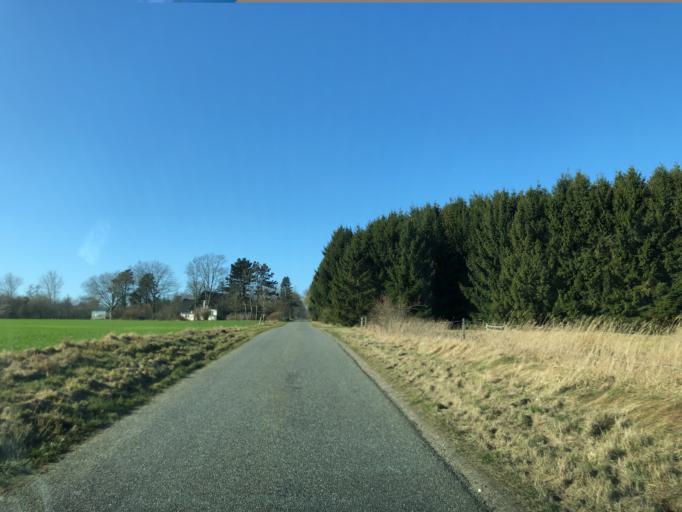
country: DK
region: Central Jutland
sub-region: Skanderborg Kommune
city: Ry
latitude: 56.1960
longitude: 9.7721
